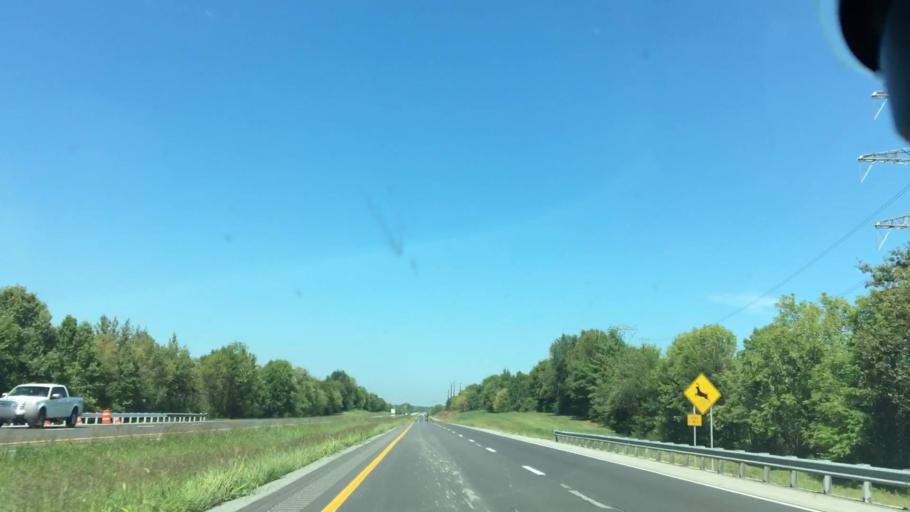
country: US
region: Kentucky
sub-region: Webster County
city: Sebree
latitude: 37.6317
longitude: -87.5090
